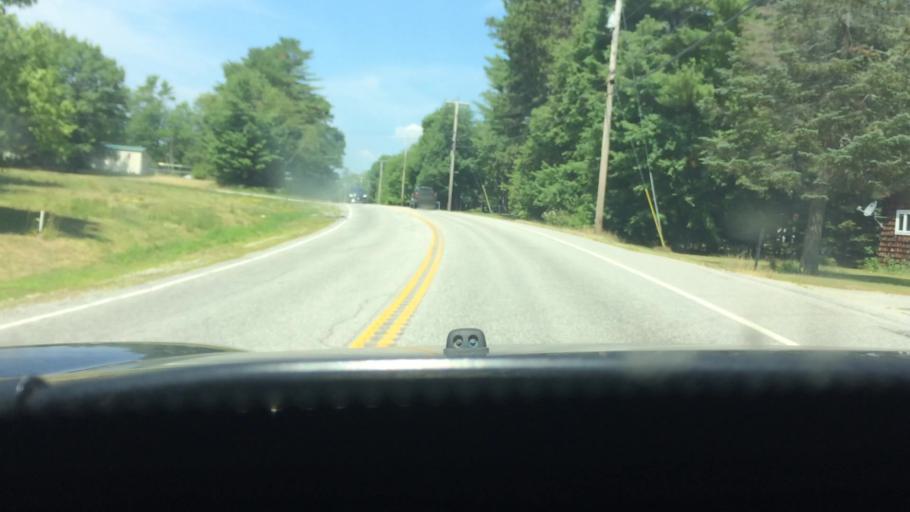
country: US
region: Maine
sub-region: Androscoggin County
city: Minot
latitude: 44.0931
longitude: -70.3485
